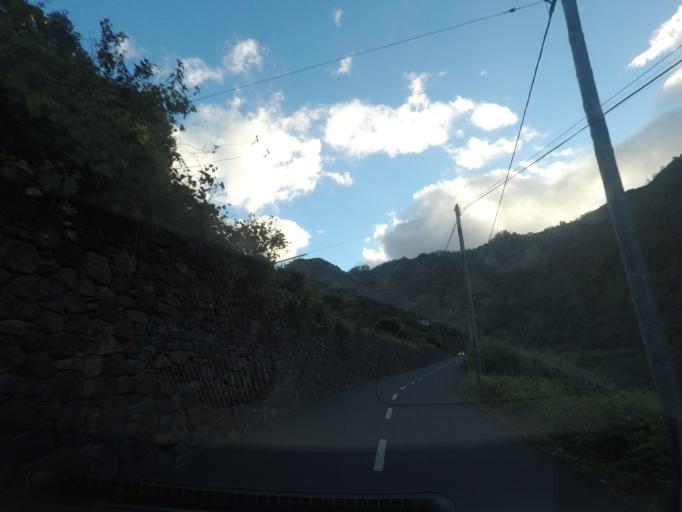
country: PT
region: Madeira
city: Ponta do Sol
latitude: 32.6916
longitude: -17.0738
